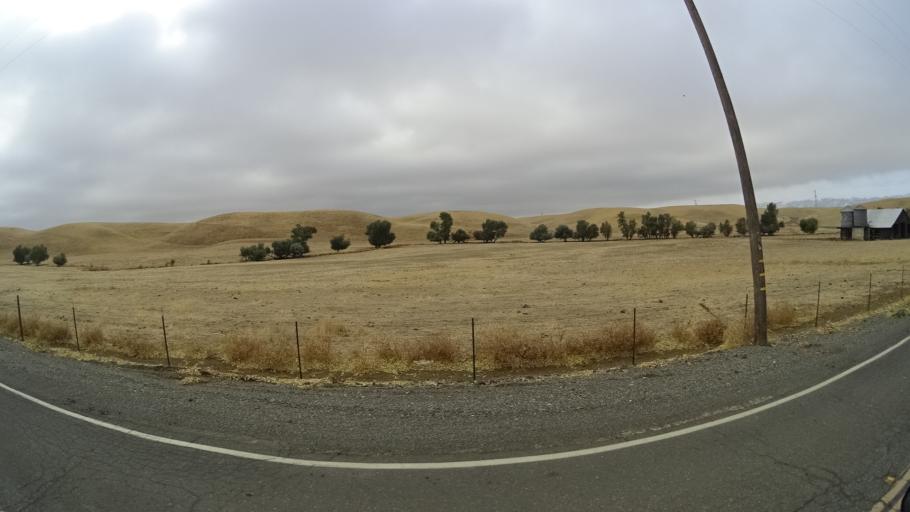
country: US
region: California
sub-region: Yolo County
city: Dunnigan
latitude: 38.8621
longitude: -122.0411
